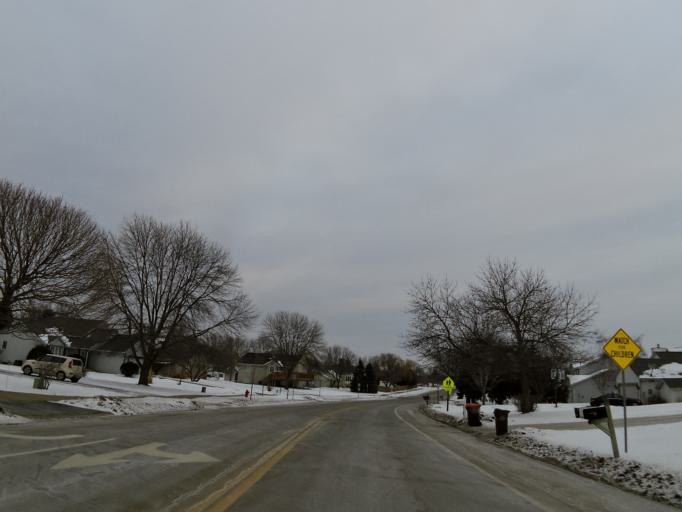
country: US
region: Minnesota
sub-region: Washington County
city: Woodbury
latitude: 44.9058
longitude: -92.9216
